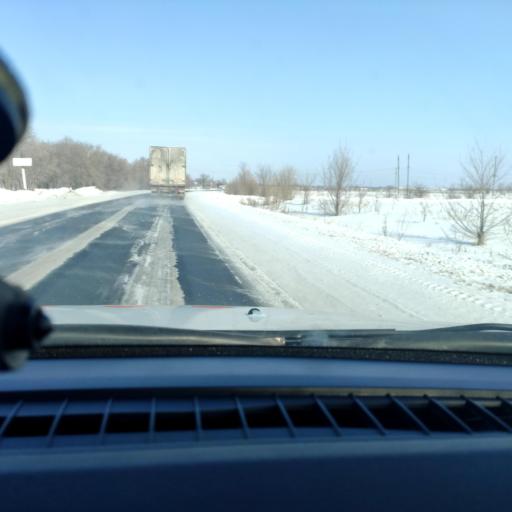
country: RU
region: Samara
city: Smyshlyayevka
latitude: 53.1735
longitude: 50.4579
